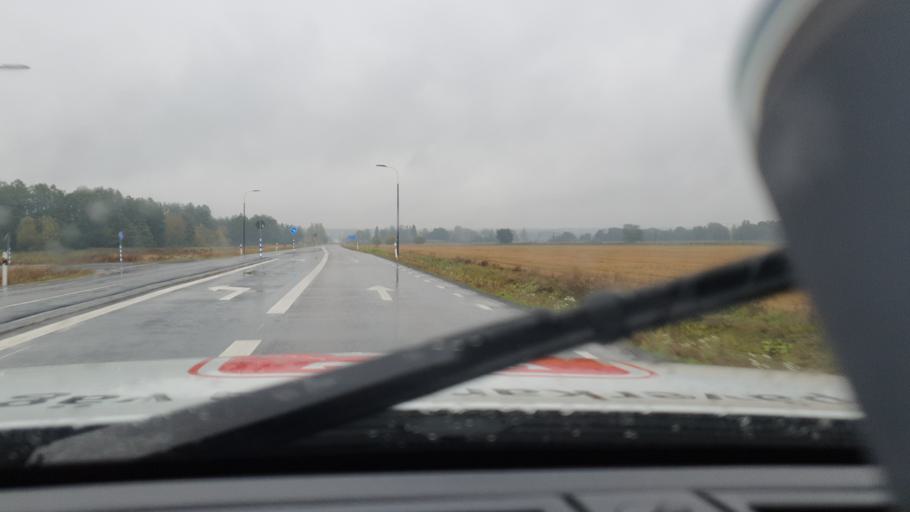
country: SE
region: Uppsala
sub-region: Tierps Kommun
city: Tierp
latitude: 60.3378
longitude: 17.5041
